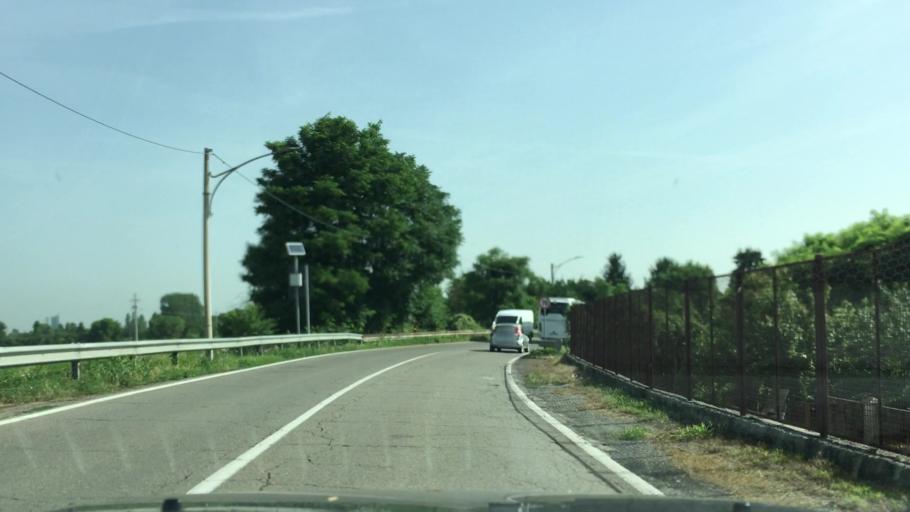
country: IT
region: Emilia-Romagna
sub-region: Provincia di Bologna
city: Progresso
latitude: 44.5431
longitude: 11.3730
